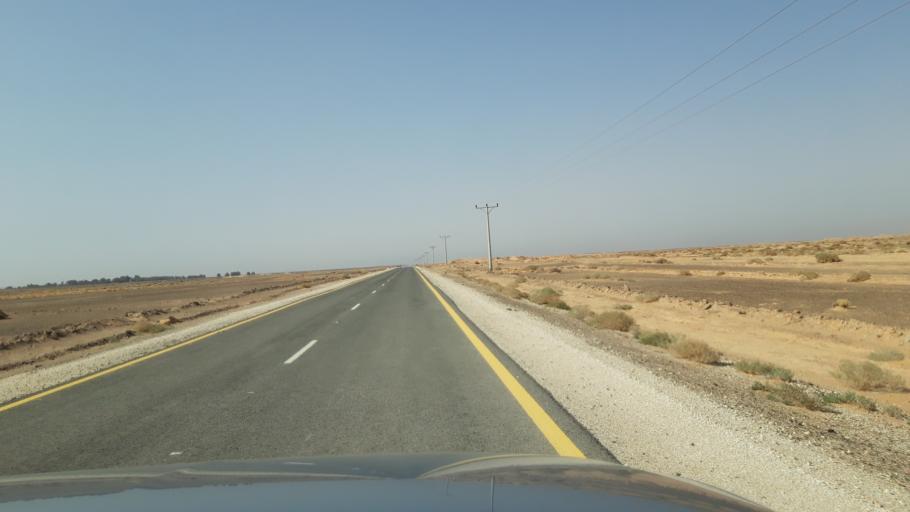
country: JO
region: Amman
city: Al Azraq ash Shamali
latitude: 31.7712
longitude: 36.7654
